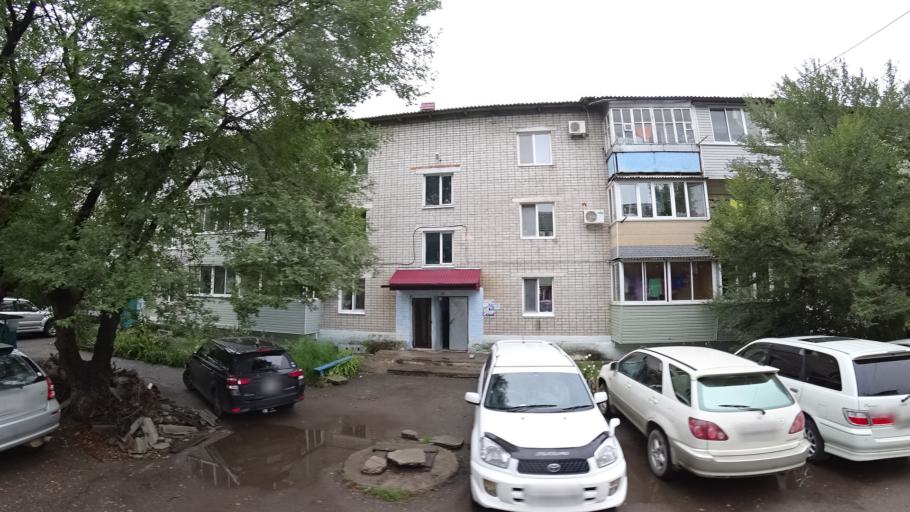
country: RU
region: Primorskiy
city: Monastyrishche
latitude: 44.1937
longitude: 132.4225
